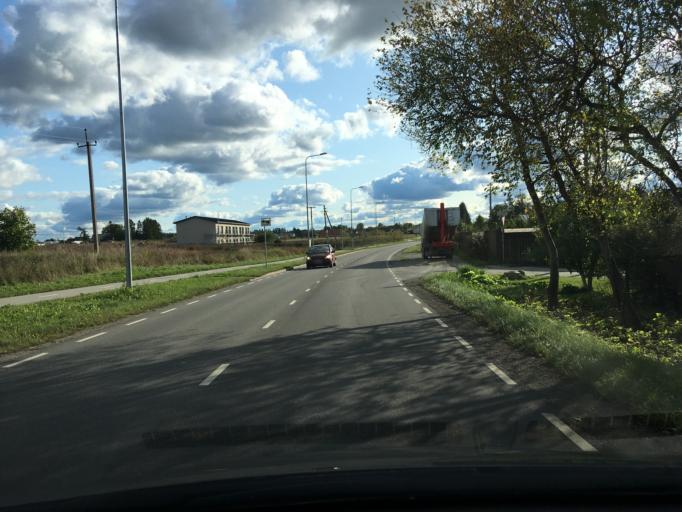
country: EE
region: Harju
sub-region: Joelaehtme vald
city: Loo
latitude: 59.4103
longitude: 24.9476
